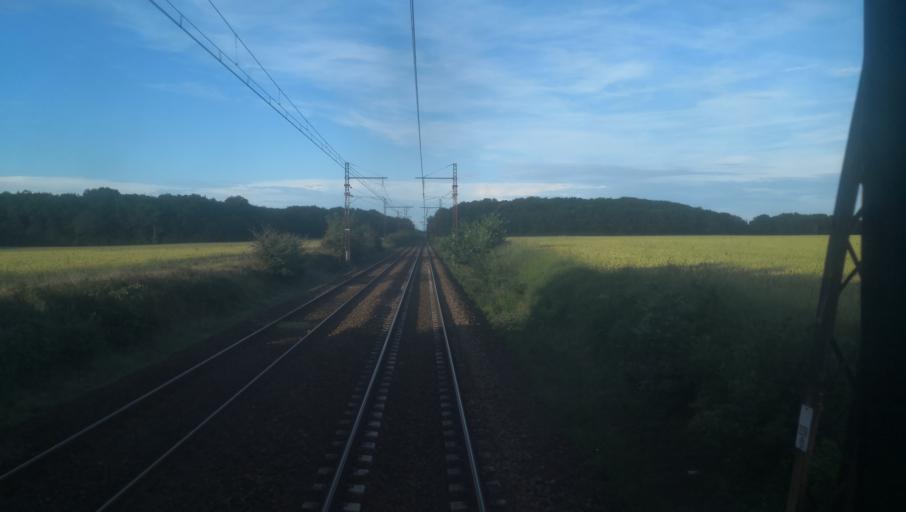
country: FR
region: Centre
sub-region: Departement de l'Indre
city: Montierchaume
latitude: 46.8316
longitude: 1.7516
